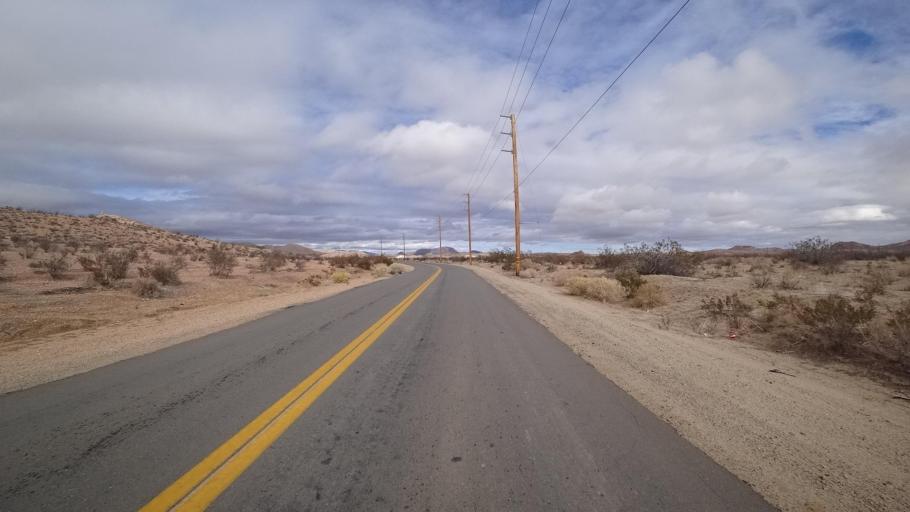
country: US
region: California
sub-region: Kern County
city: Rosamond
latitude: 34.8789
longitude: -118.2252
